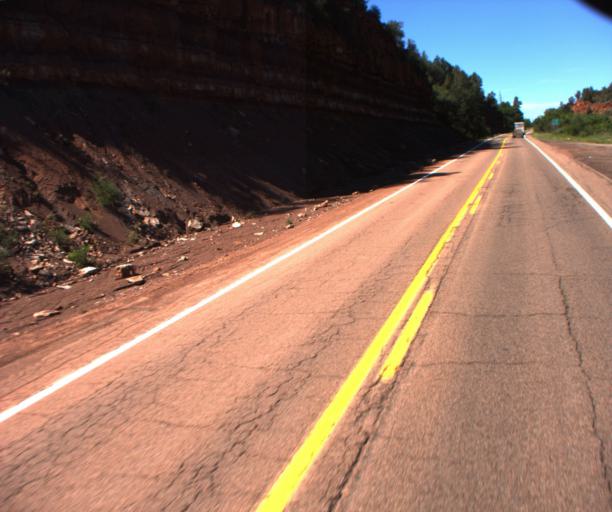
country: US
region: Arizona
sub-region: Navajo County
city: Cibecue
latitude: 33.9794
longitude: -110.3084
